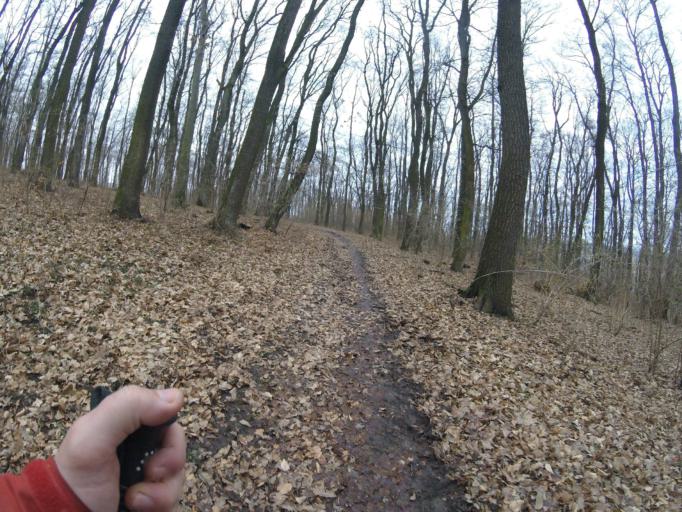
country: HU
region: Veszprem
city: Zirc
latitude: 47.3368
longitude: 17.9015
